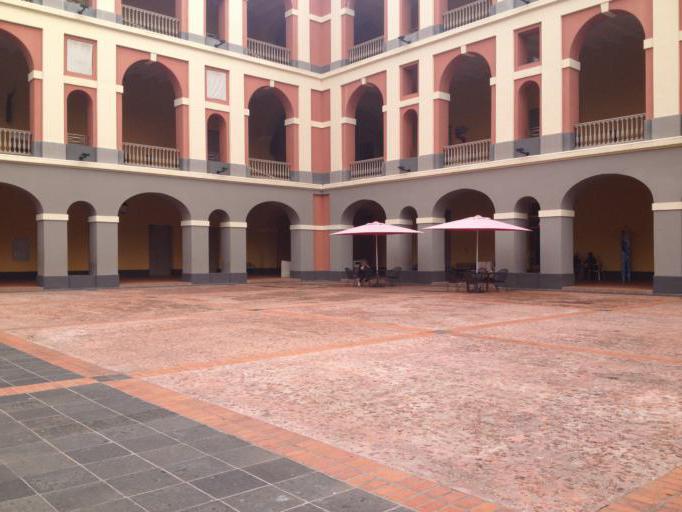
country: PR
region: San Juan
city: San Juan
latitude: 18.4678
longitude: -66.1197
